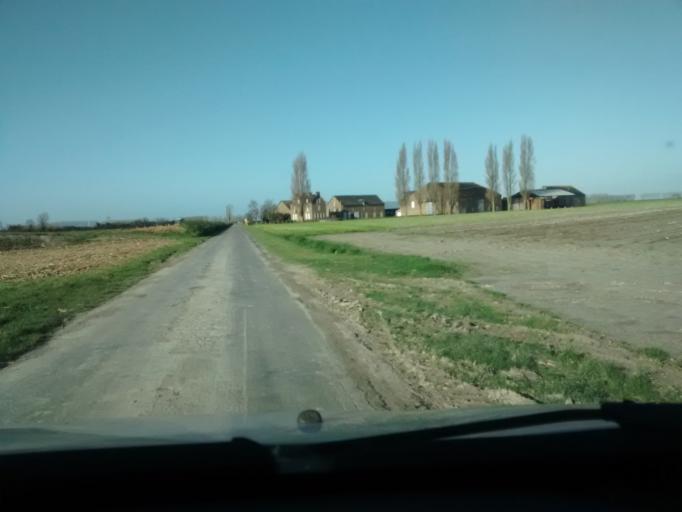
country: FR
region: Brittany
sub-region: Departement d'Ille-et-Vilaine
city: Roz-sur-Couesnon
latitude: 48.5979
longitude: -1.5652
